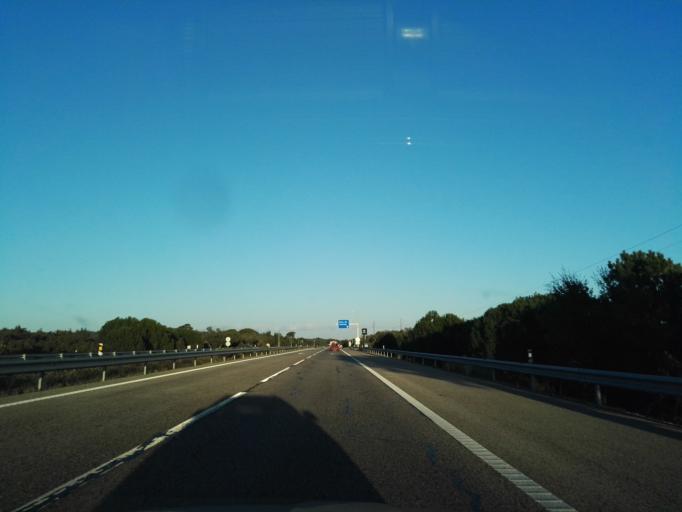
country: PT
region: Evora
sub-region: Vendas Novas
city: Vendas Novas
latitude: 38.6192
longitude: -8.5857
